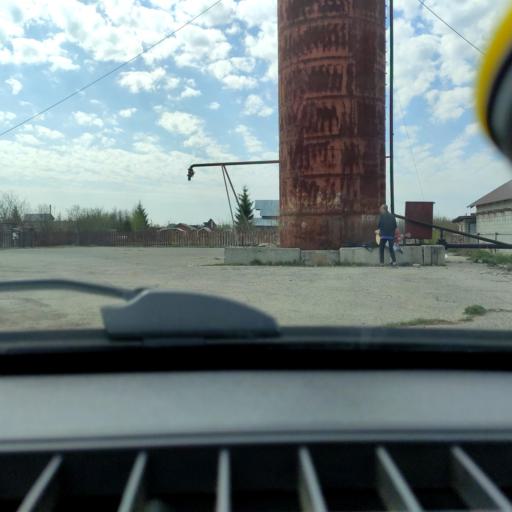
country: RU
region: Samara
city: Tol'yatti
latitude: 53.6982
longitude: 49.4511
